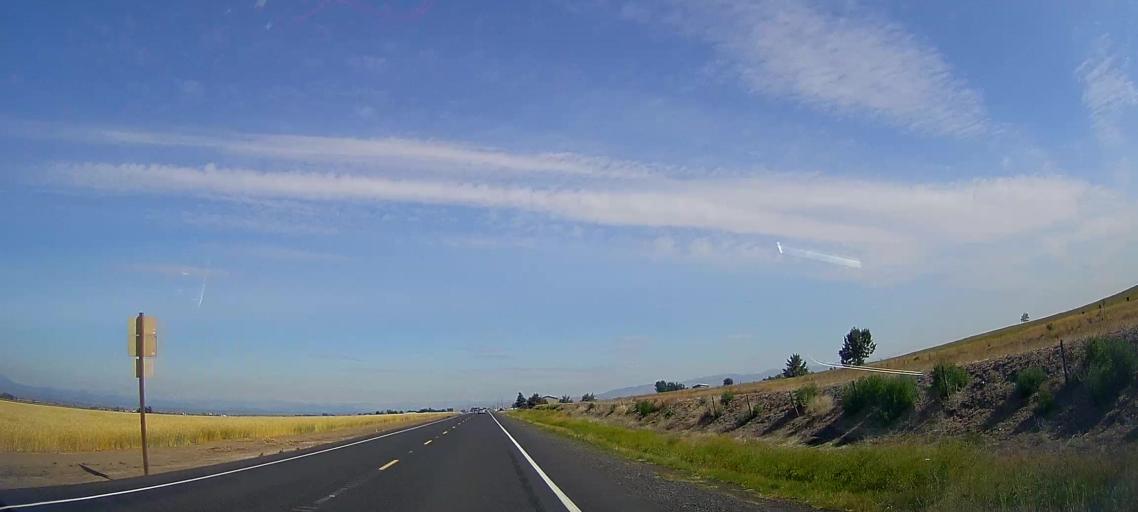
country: US
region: Oregon
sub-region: Jefferson County
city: Madras
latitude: 44.6717
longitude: -121.1409
